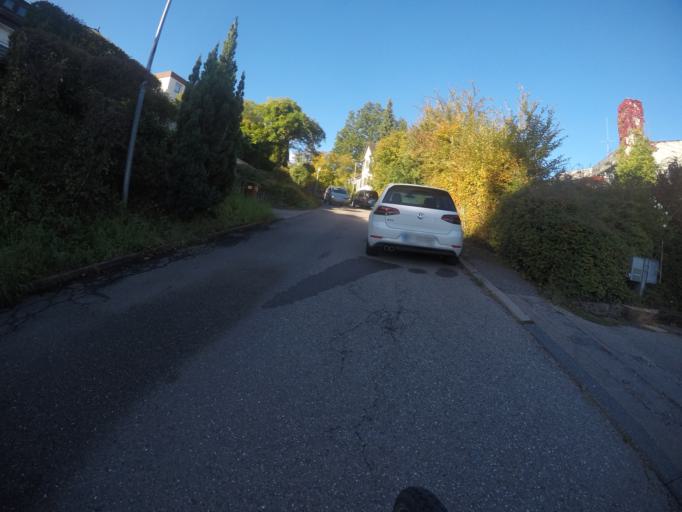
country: DE
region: Baden-Wuerttemberg
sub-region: Regierungsbezirk Stuttgart
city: Steinenbronn
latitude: 48.7161
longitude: 9.1026
